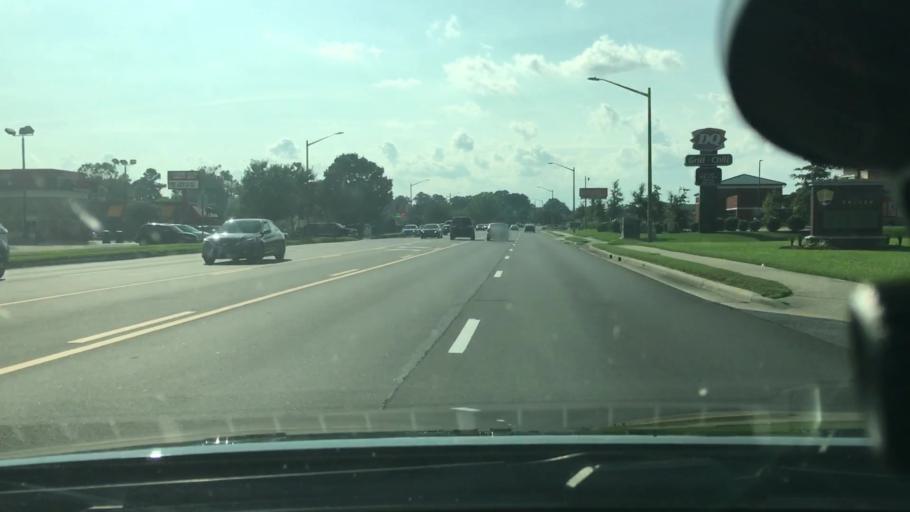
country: US
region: North Carolina
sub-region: Pitt County
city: Greenville
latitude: 35.5986
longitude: -77.3292
